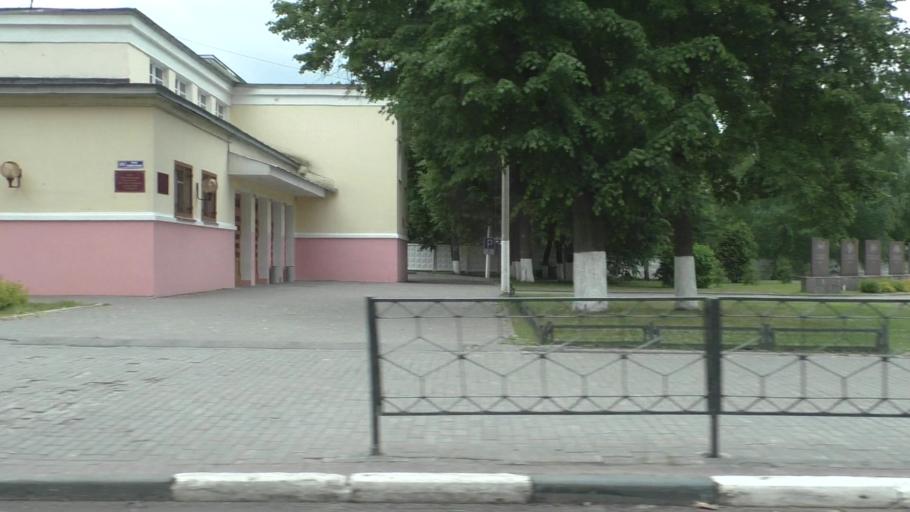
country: RU
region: Moskovskaya
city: Yegor'yevsk
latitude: 55.3765
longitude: 39.0458
